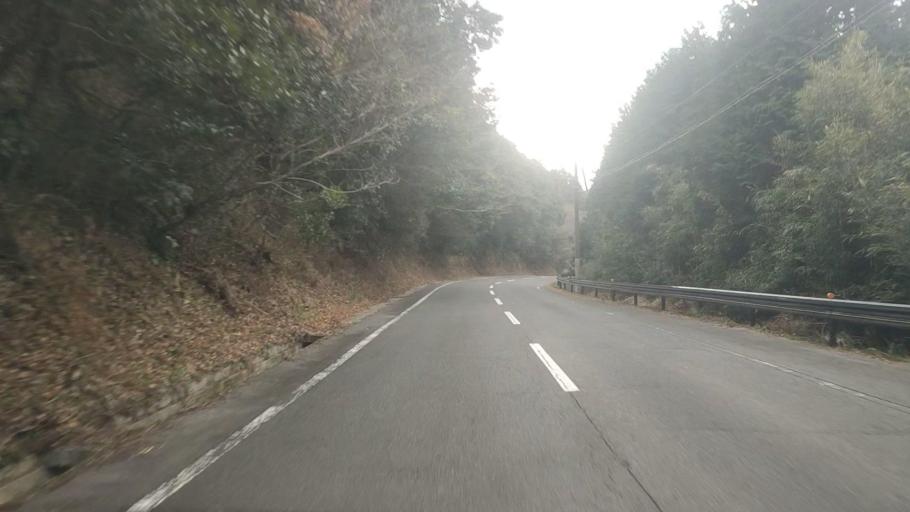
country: JP
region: Nagasaki
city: Shimabara
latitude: 32.7223
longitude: 130.2495
